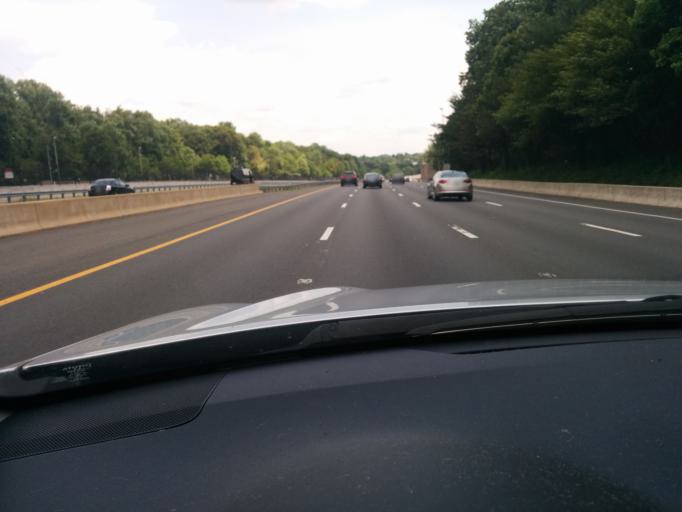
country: US
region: Virginia
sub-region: Fairfax County
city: Wolf Trap
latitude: 38.9476
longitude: -77.3020
